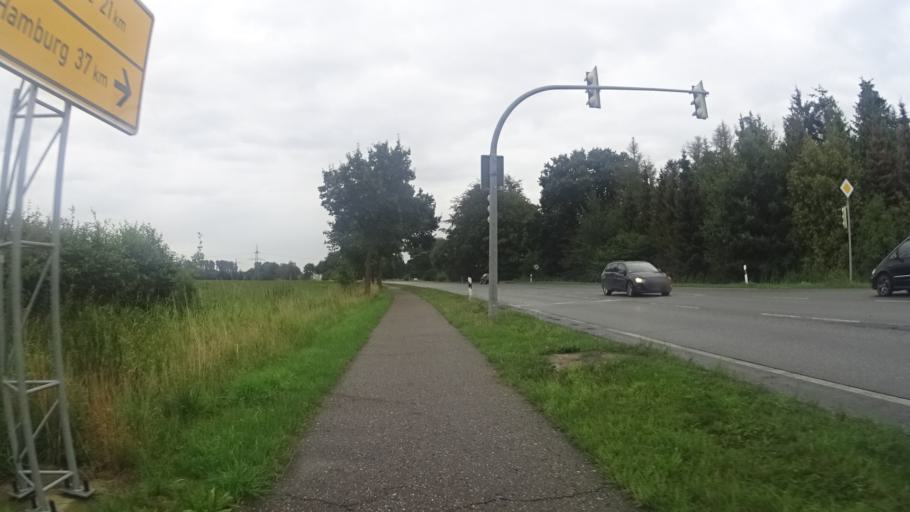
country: DE
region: Schleswig-Holstein
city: Kiebitzreihe
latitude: 53.7817
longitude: 9.6402
